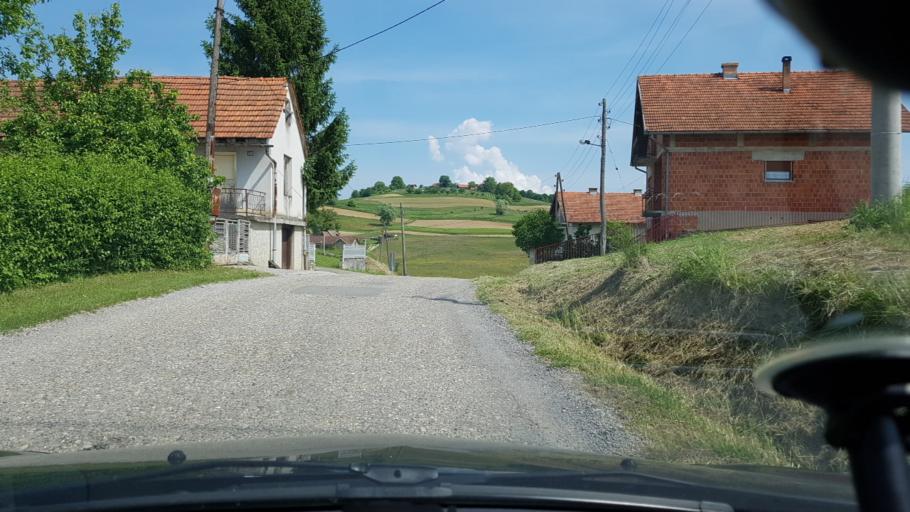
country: HR
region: Krapinsko-Zagorska
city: Selnica
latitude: 46.0092
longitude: 16.0734
